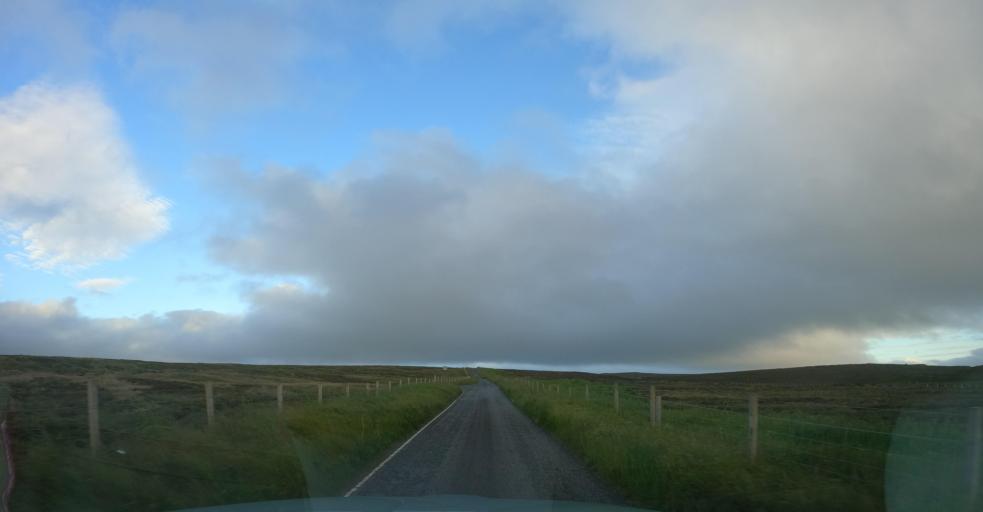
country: GB
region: Scotland
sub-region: Eilean Siar
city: Stornoway
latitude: 58.2074
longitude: -6.2496
